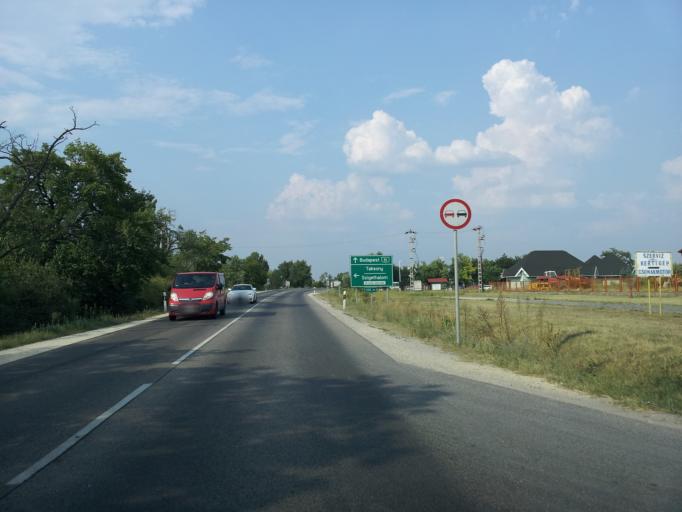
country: HU
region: Pest
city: Szigethalom
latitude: 47.3050
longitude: 19.0353
